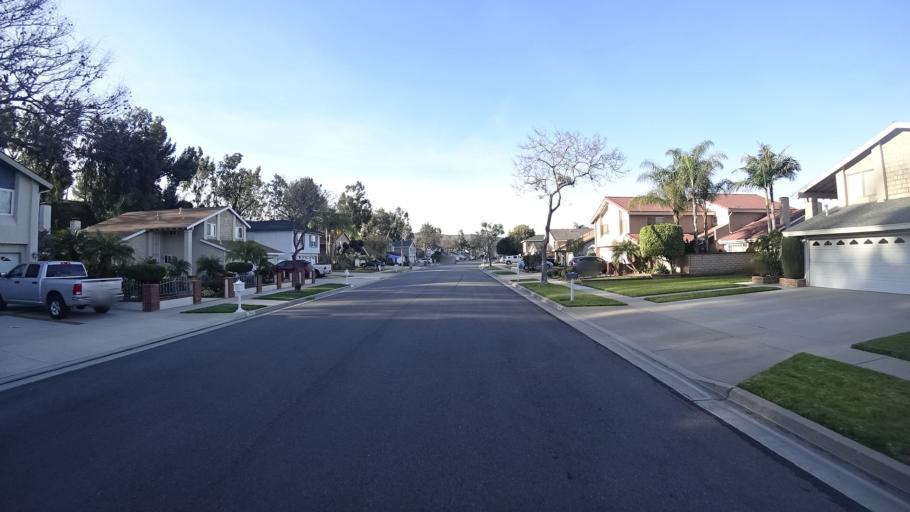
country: US
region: California
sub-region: Orange County
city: Yorba Linda
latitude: 33.8636
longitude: -117.7651
